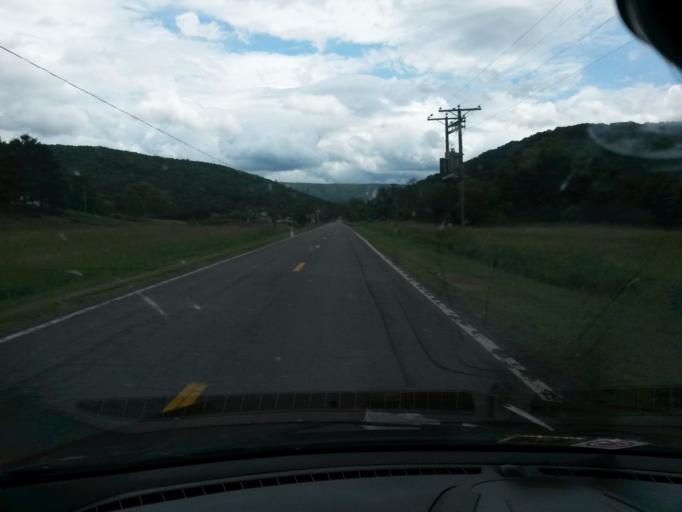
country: US
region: West Virginia
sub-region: Monroe County
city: Union
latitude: 37.5729
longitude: -80.4191
